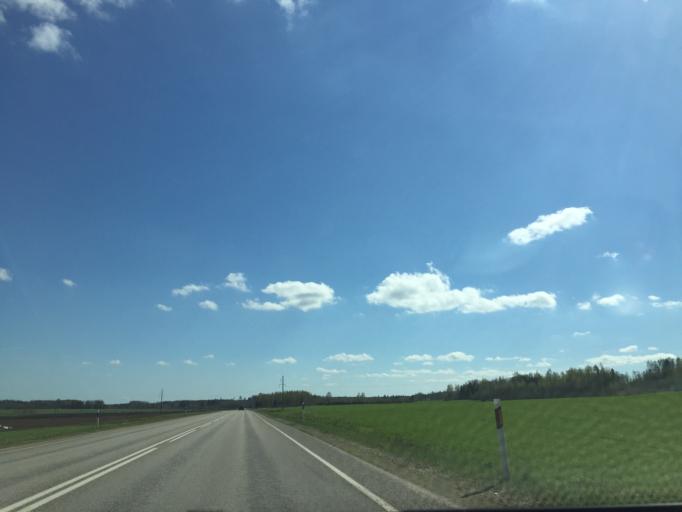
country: EE
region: Valgamaa
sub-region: Valga linn
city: Valga
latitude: 57.8836
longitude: 26.0589
